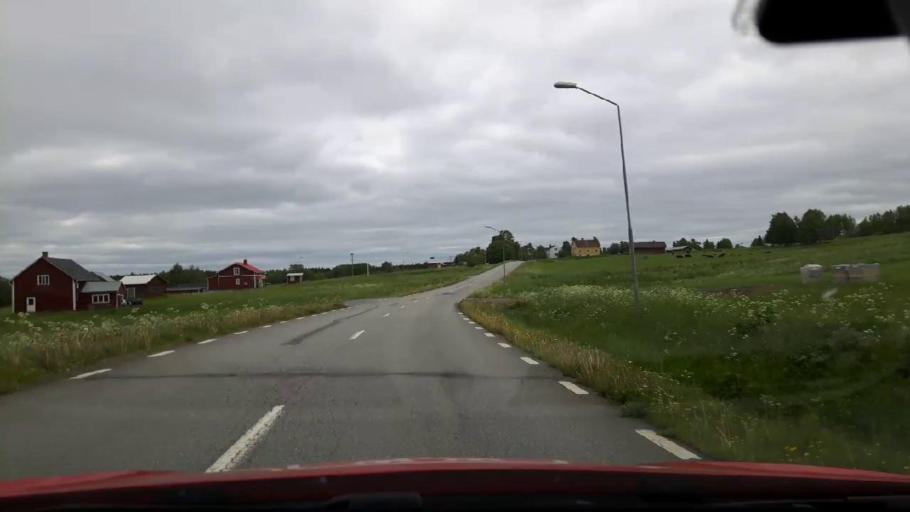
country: SE
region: Jaemtland
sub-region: Stroemsunds Kommun
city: Stroemsund
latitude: 63.5586
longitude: 15.4010
